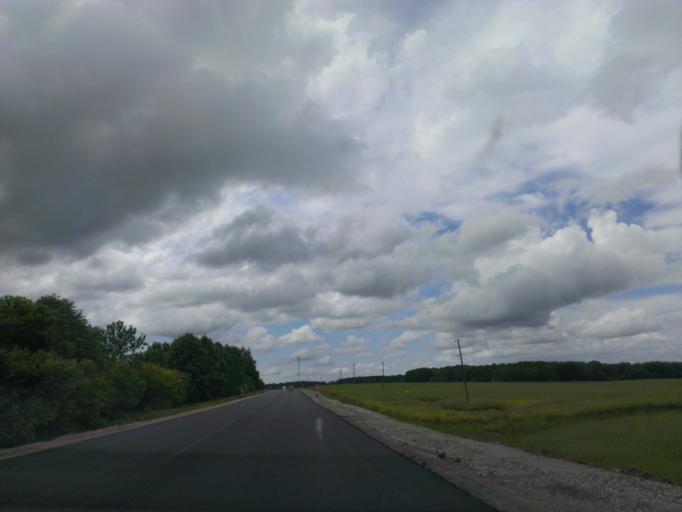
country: LV
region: Durbe
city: Liegi
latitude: 56.5898
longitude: 21.4165
